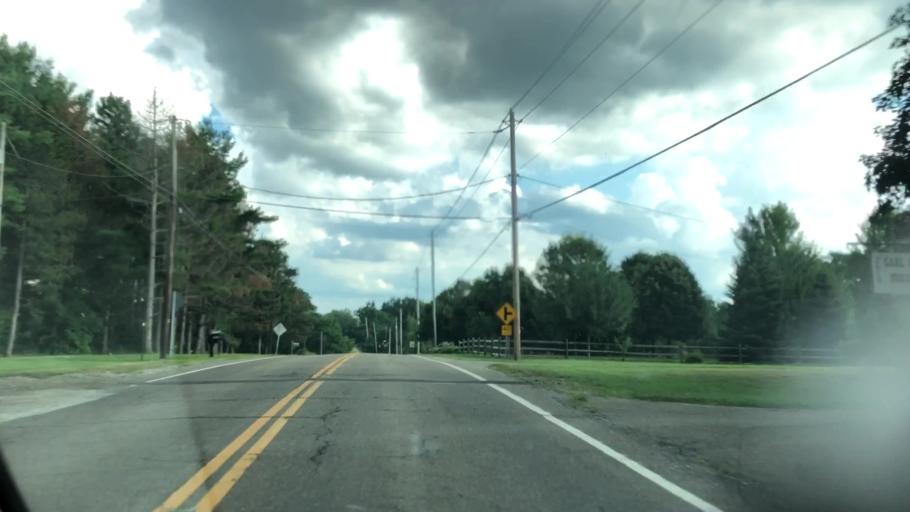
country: US
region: Ohio
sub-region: Summit County
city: Norton
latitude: 41.0671
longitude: -81.6389
